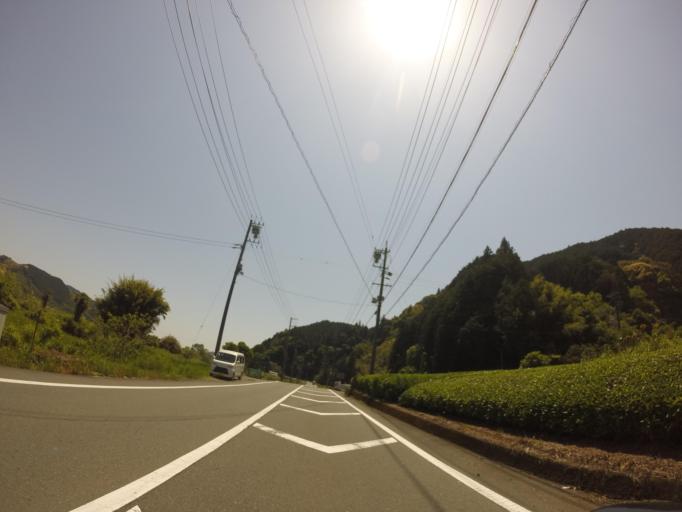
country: JP
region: Shizuoka
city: Shizuoka-shi
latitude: 34.9910
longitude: 138.2884
